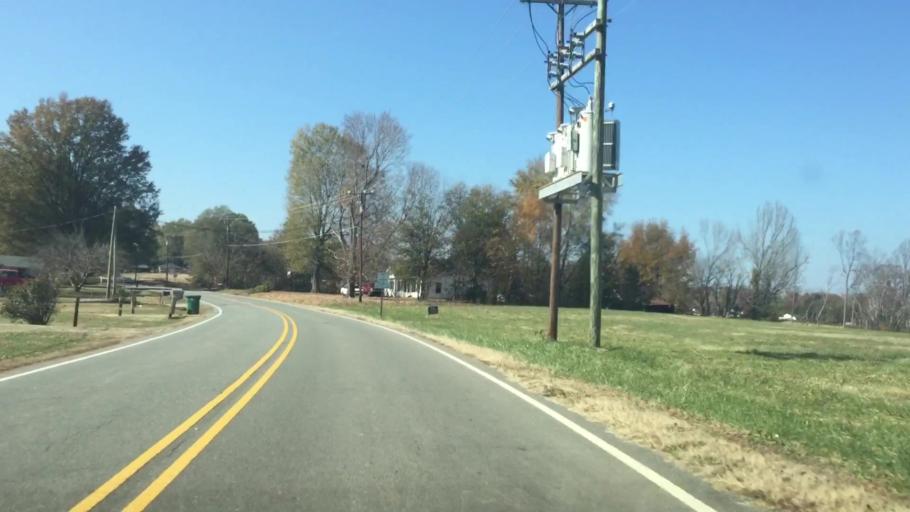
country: US
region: North Carolina
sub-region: Rockingham County
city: Reidsville
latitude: 36.3304
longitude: -79.6172
